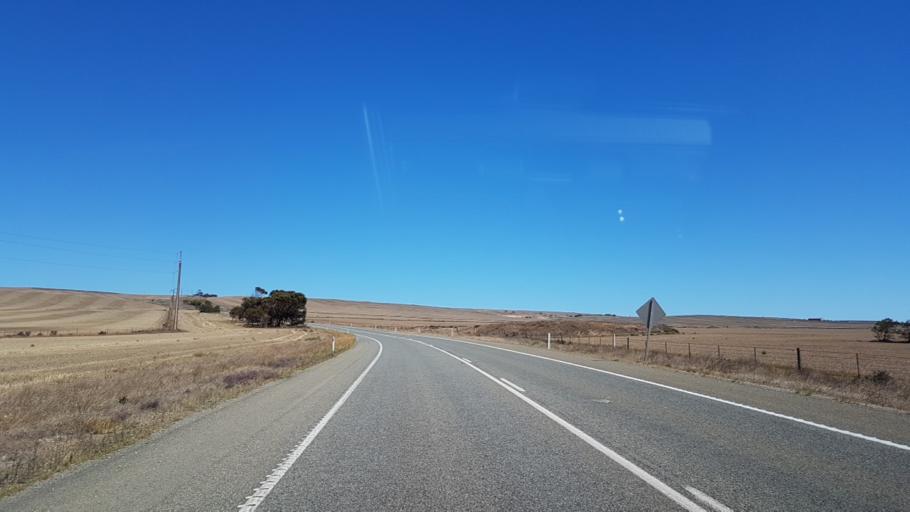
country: AU
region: South Australia
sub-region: Wakefield
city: Balaklava
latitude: -34.0719
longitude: 138.0713
